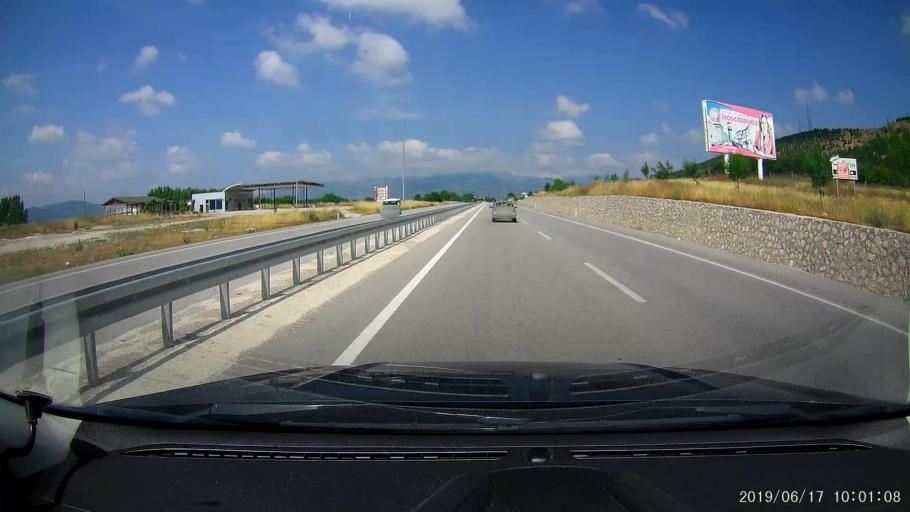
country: TR
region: Amasya
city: Gumushacikoy
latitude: 40.8665
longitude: 35.2722
